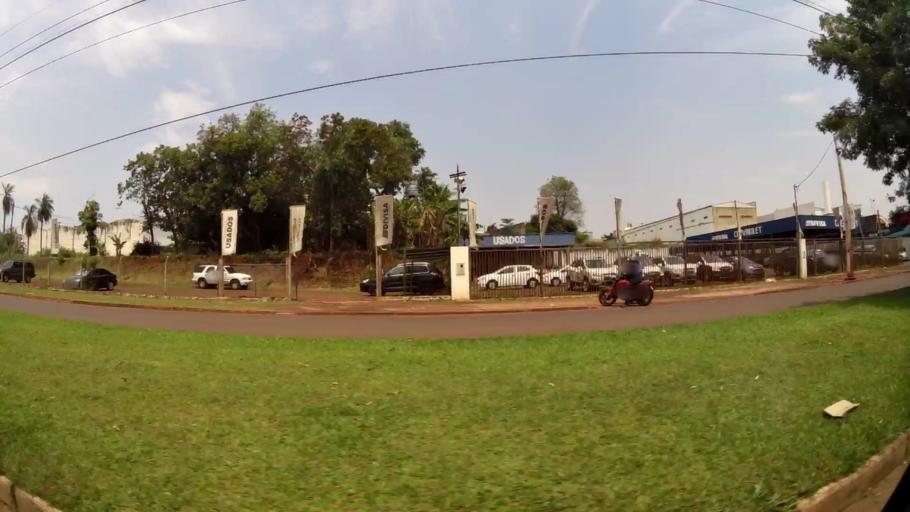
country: PY
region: Alto Parana
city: Ciudad del Este
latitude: -25.4984
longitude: -54.6332
